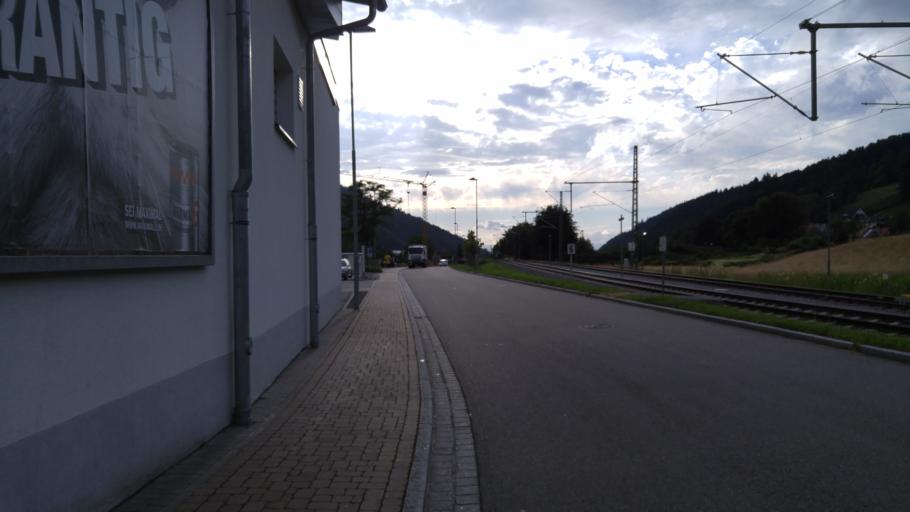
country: DE
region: Baden-Wuerttemberg
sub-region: Freiburg Region
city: Muenstertal/Schwarzwald
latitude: 47.8552
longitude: 7.7800
